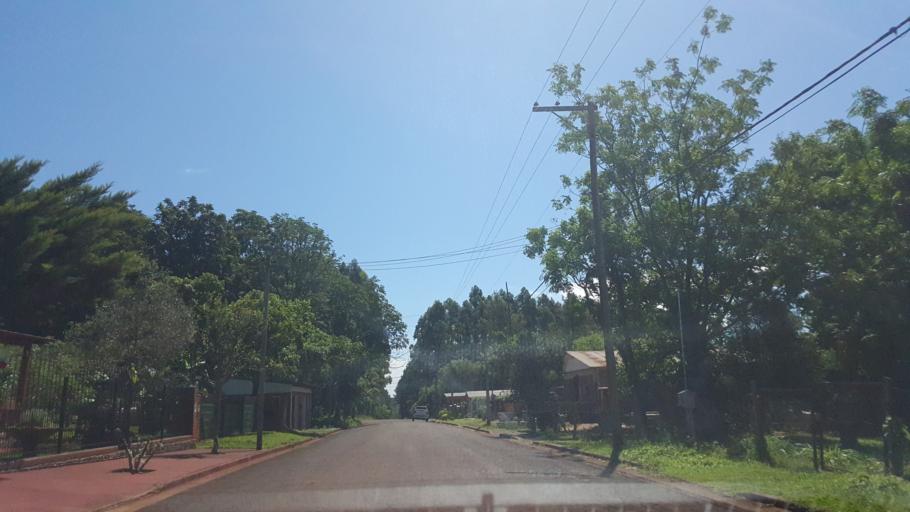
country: AR
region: Misiones
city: Capiovi
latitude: -26.9318
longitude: -55.0641
